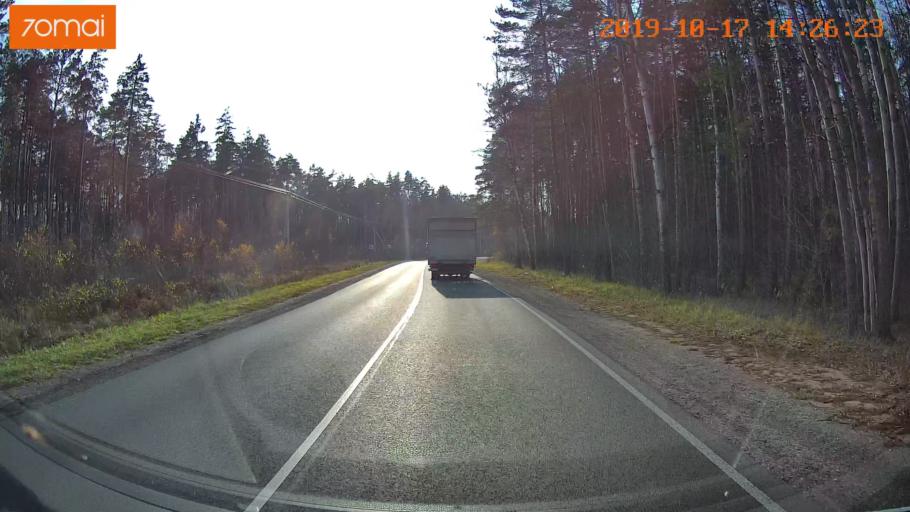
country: RU
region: Moskovskaya
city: Radovitskiy
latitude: 54.9925
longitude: 39.9678
